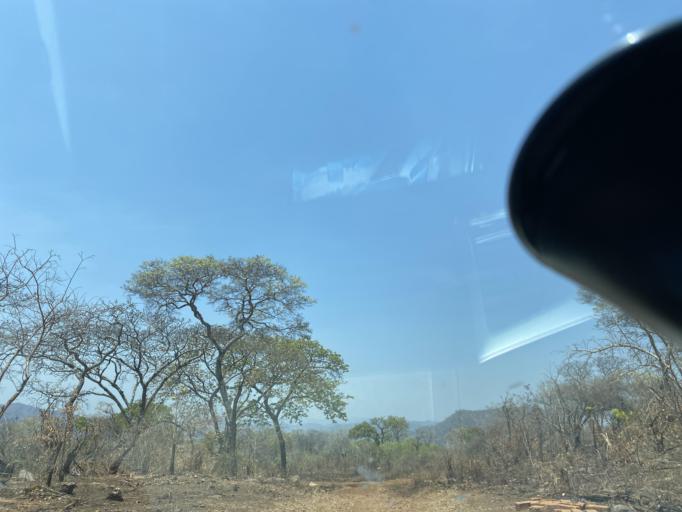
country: ZM
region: Lusaka
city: Kafue
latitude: -15.8046
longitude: 28.4463
